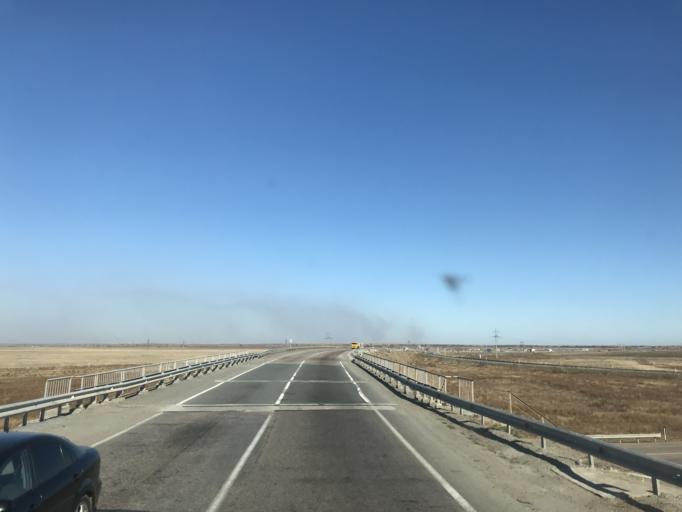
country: KZ
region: Pavlodar
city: Leninskiy
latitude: 52.1533
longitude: 76.8211
